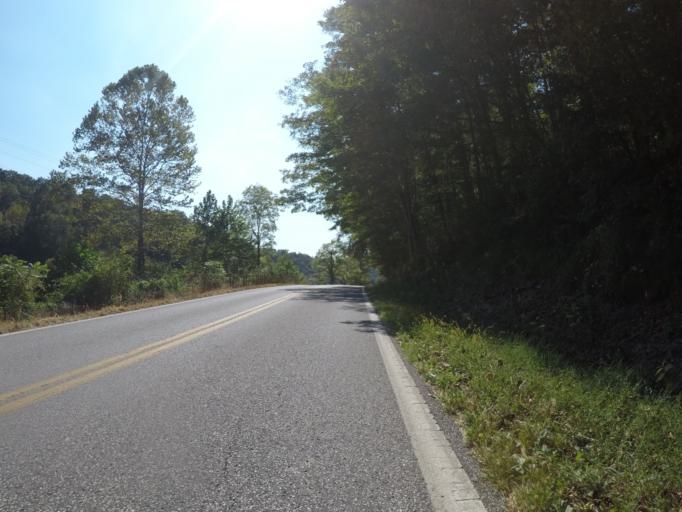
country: US
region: West Virginia
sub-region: Cabell County
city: Lesage
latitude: 38.5592
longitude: -82.3927
